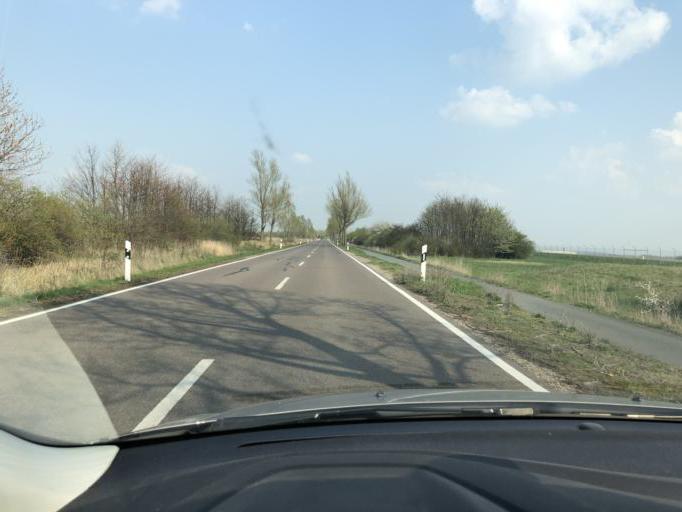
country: DE
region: Saxony
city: Zwochau
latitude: 51.4364
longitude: 12.2603
